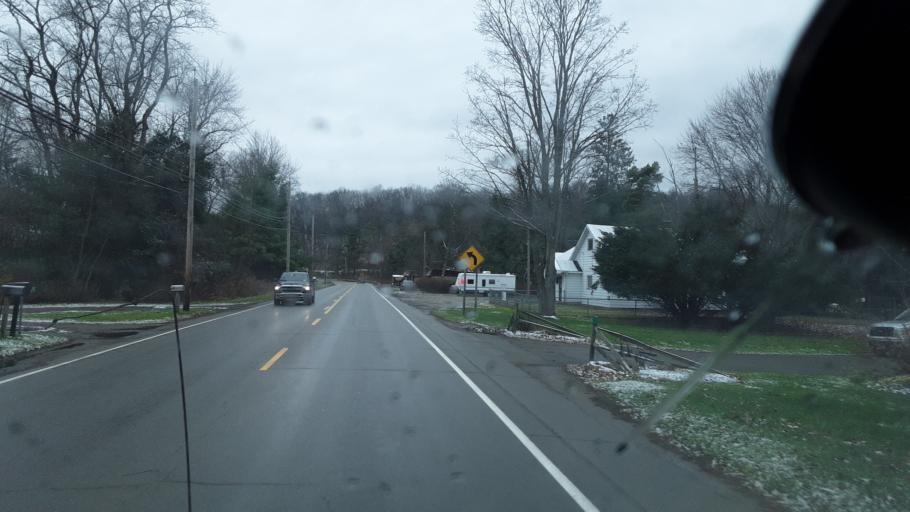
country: US
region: New York
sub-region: Cattaraugus County
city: Westons Mills
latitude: 42.0534
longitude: -78.3583
